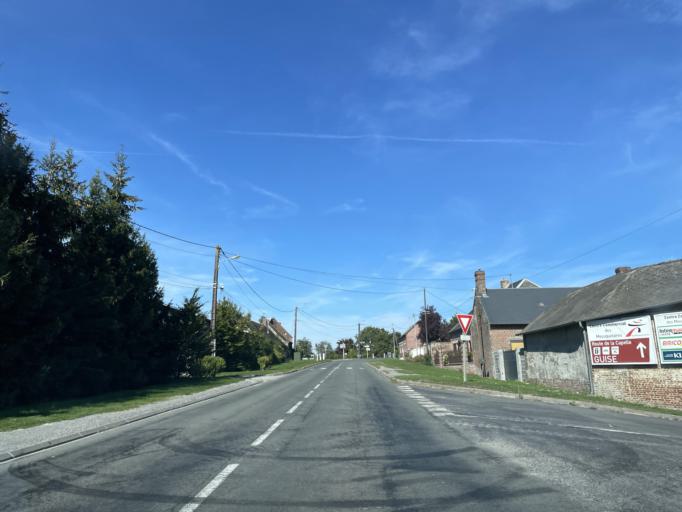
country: FR
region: Picardie
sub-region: Departement de l'Aisne
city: Guise
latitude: 49.8190
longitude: 3.6454
